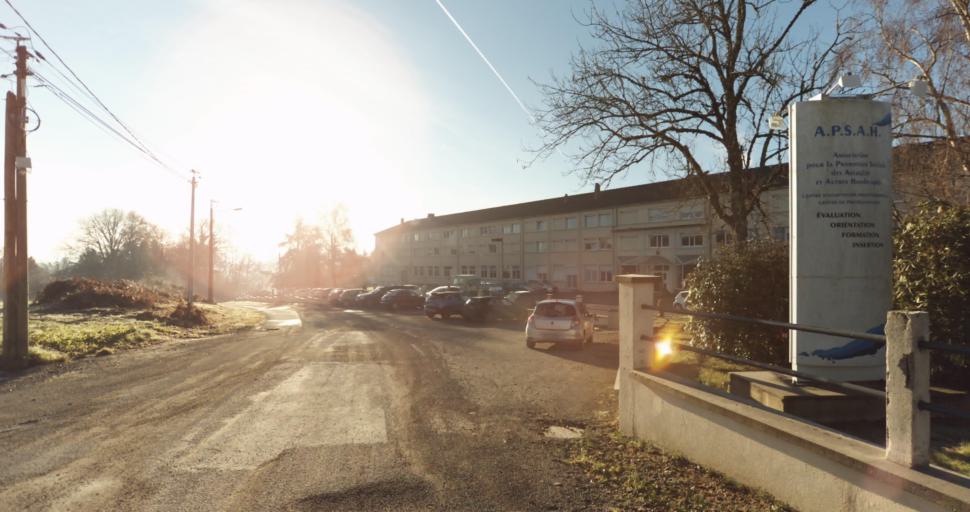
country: FR
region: Limousin
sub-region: Departement de la Haute-Vienne
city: Aixe-sur-Vienne
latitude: 45.8118
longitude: 1.1371
